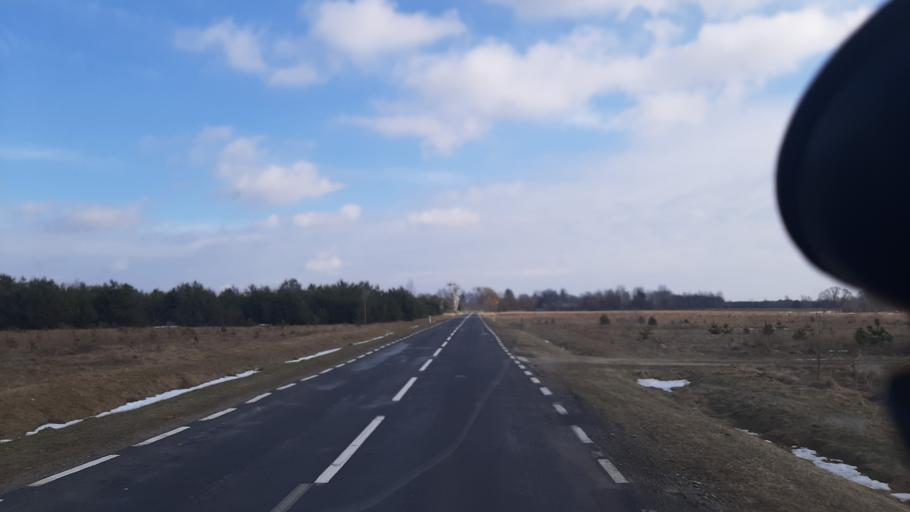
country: PL
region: Lublin Voivodeship
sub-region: Powiat wlodawski
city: Urszulin
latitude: 51.4987
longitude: 23.2033
